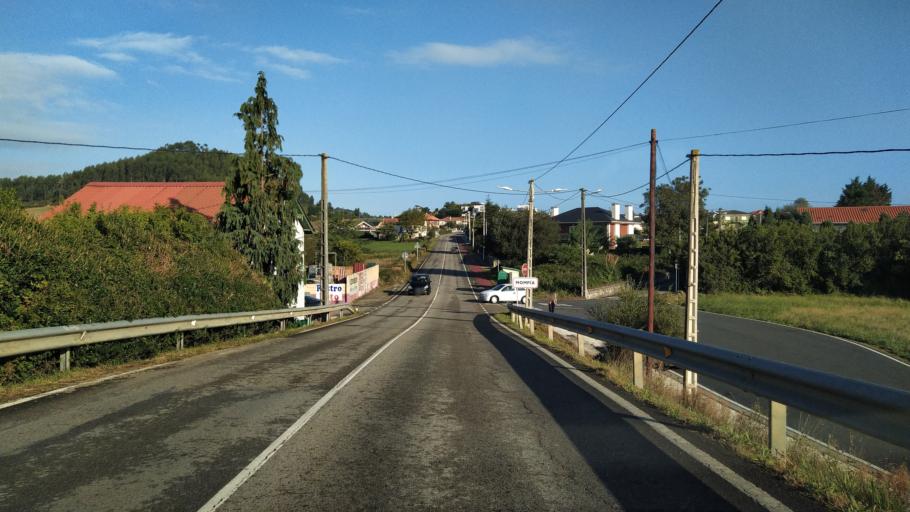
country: ES
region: Cantabria
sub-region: Provincia de Cantabria
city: Santa Cruz de Bezana
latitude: 43.4354
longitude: -3.9186
